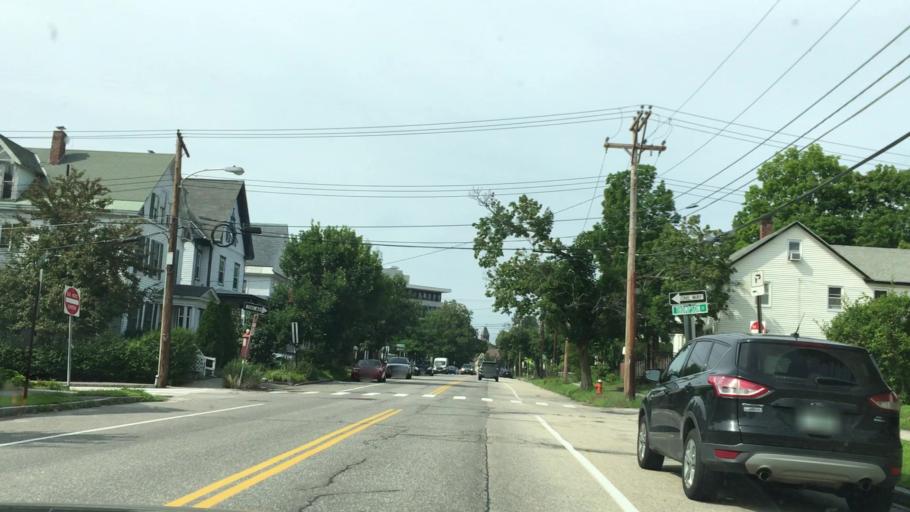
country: US
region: New Hampshire
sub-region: Merrimack County
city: Concord
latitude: 43.1999
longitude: -71.5390
